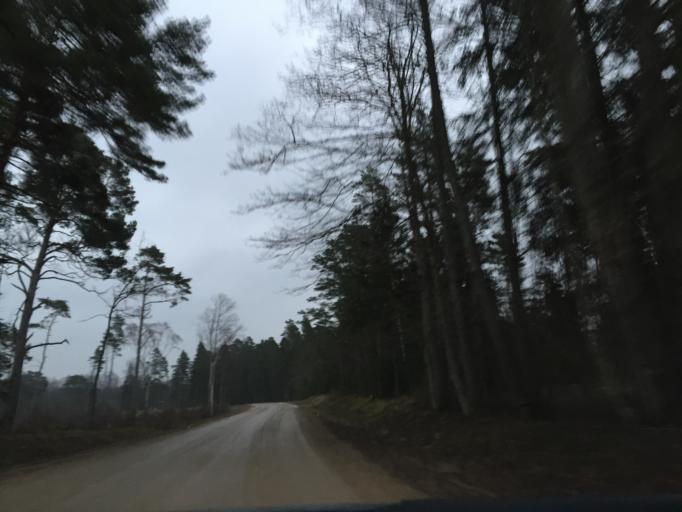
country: EE
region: Saare
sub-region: Kuressaare linn
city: Kuressaare
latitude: 58.6003
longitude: 22.5183
